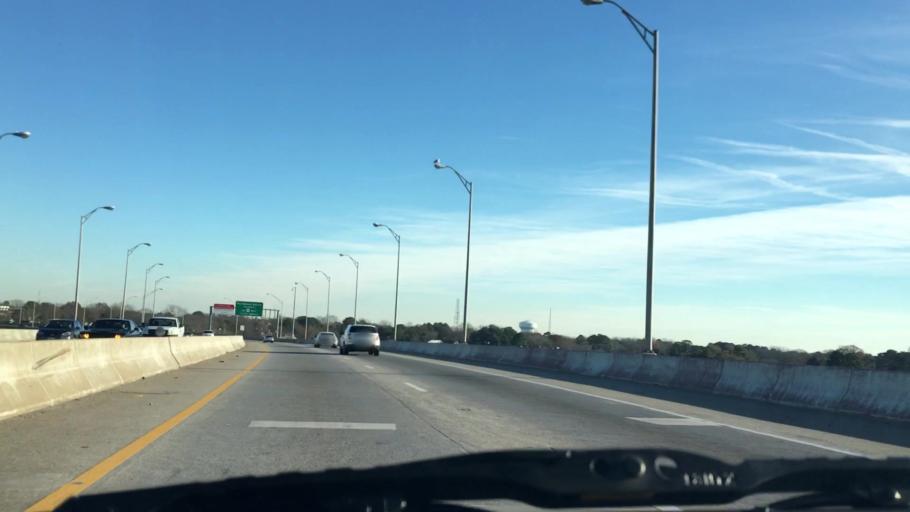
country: US
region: Virginia
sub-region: City of Portsmouth
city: Portsmouth Heights
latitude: 36.8560
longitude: -76.3456
